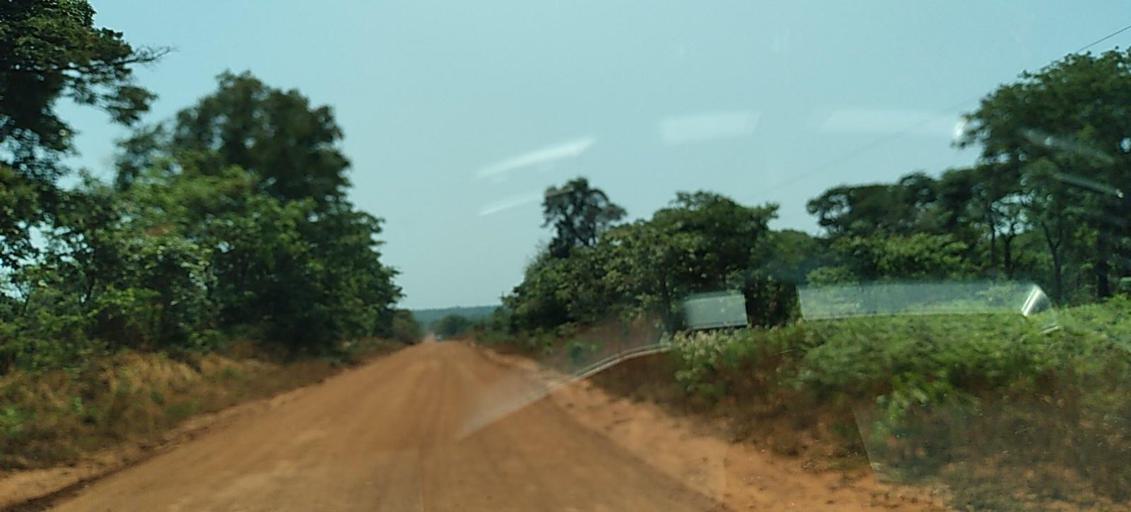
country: ZM
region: North-Western
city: Kansanshi
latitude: -11.9901
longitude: 26.8399
